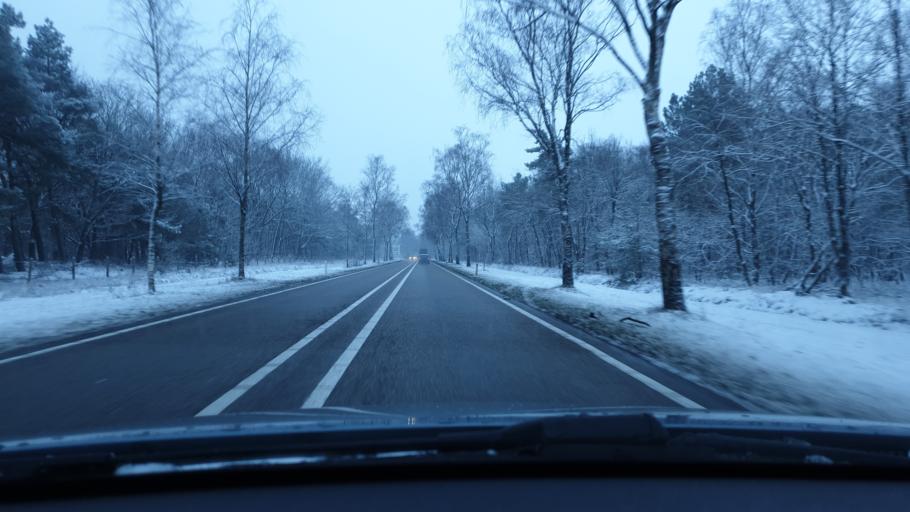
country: NL
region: North Brabant
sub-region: Gemeente Landerd
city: Reek
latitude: 51.7338
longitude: 5.6695
